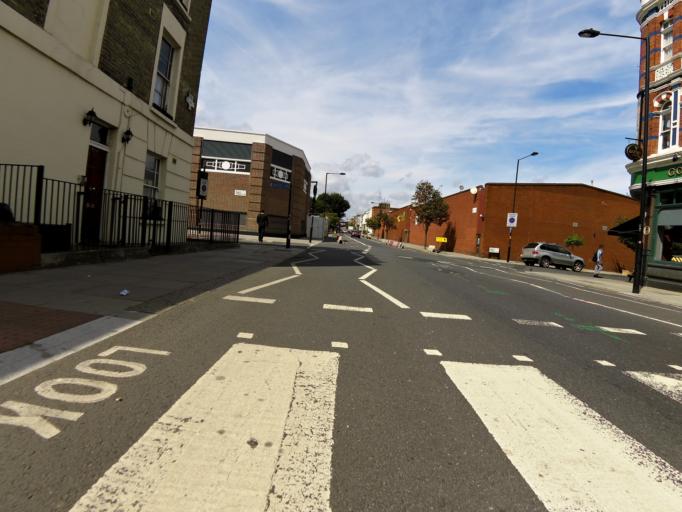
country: GB
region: England
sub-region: Greater London
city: Camden Town
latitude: 51.5389
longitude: -0.1360
